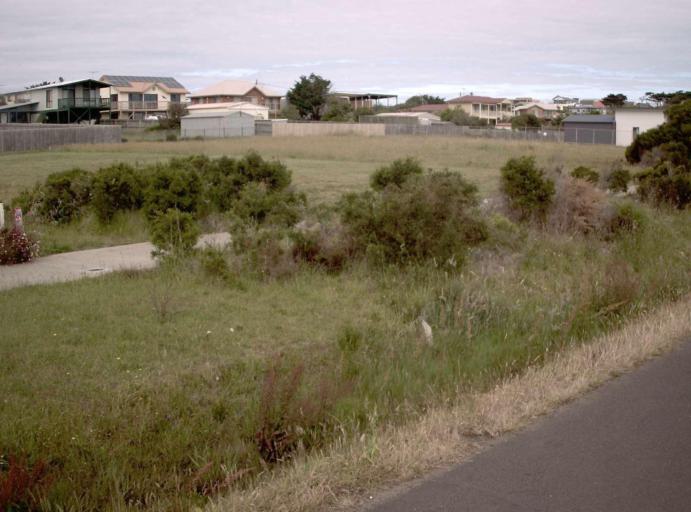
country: AU
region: Victoria
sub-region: Bass Coast
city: Phillip Island
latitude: -38.5101
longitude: 145.2959
